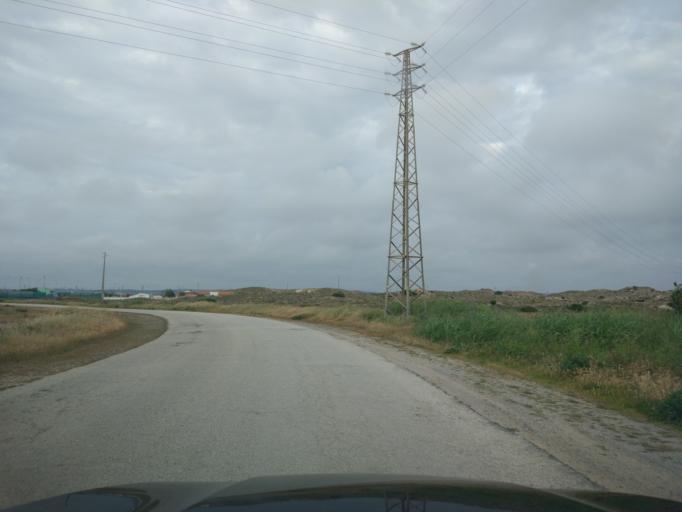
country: PT
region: Leiria
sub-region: Peniche
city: Peniche
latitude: 39.3490
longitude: -9.3620
